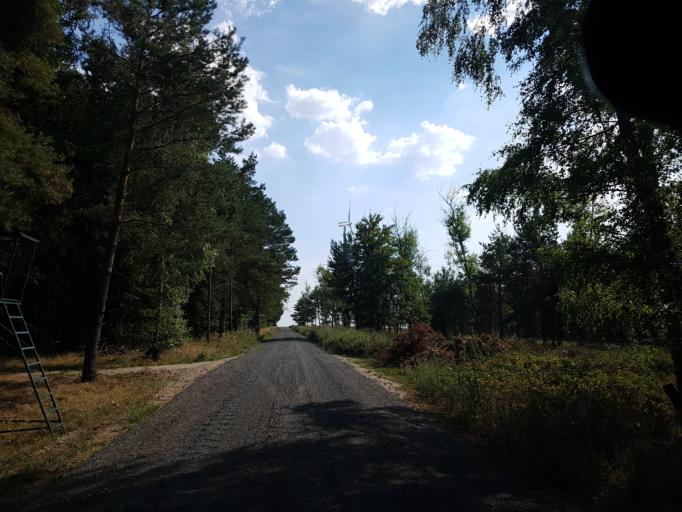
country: DE
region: Brandenburg
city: Treuenbrietzen
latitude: 52.0127
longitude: 12.8621
